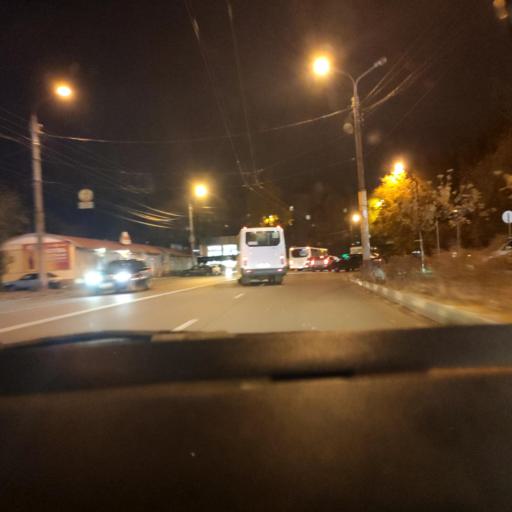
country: RU
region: Voronezj
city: Podgornoye
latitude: 51.7068
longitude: 39.1479
